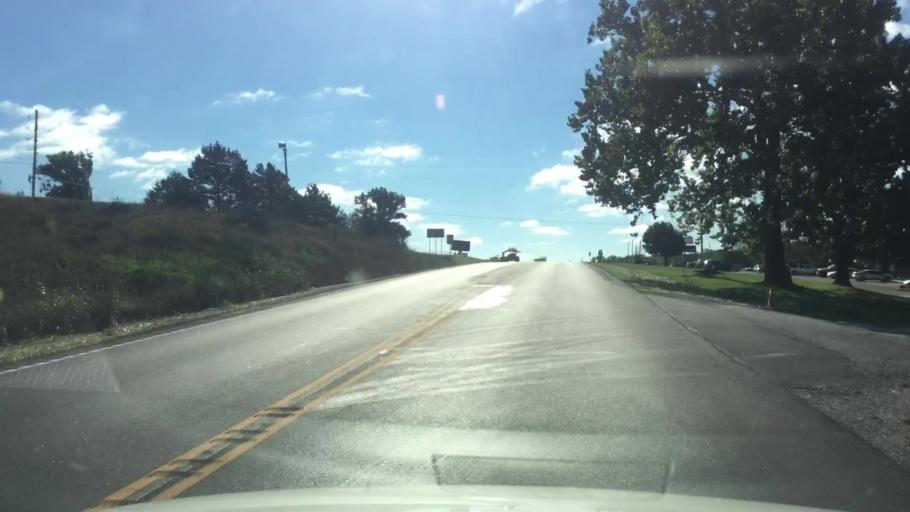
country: US
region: Missouri
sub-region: Boone County
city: Columbia
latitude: 38.9755
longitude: -92.4351
